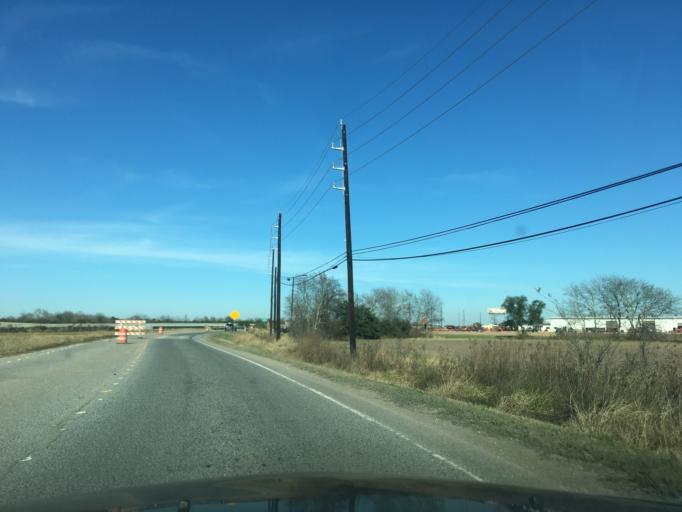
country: US
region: Texas
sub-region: Fort Bend County
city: Rosenberg
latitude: 29.5230
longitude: -95.8718
